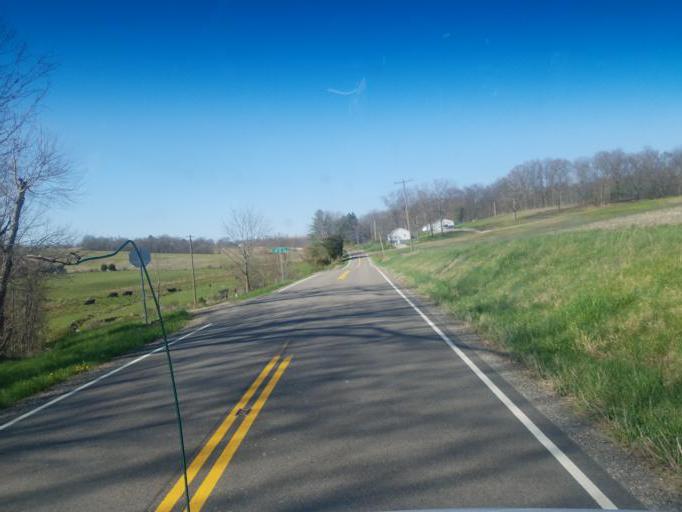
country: US
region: Ohio
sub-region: Muskingum County
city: Frazeysburg
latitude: 40.2606
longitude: -82.1194
